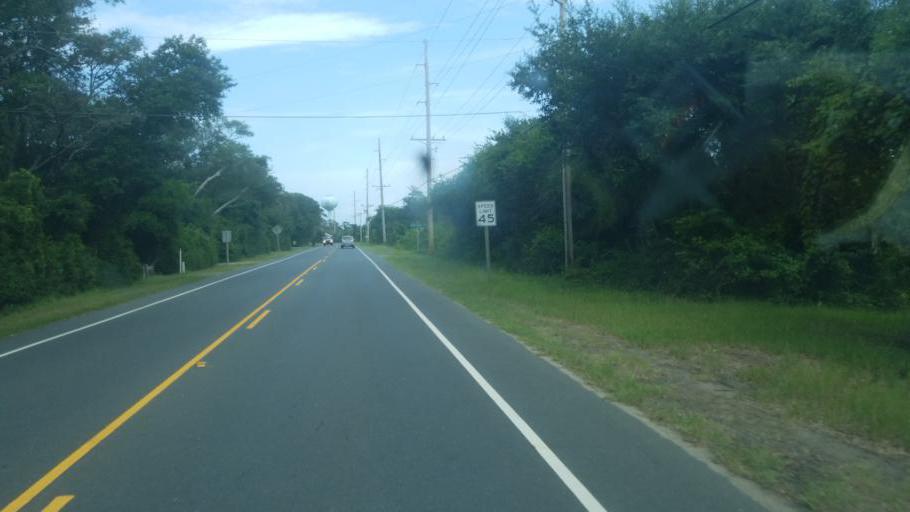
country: US
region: North Carolina
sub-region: Dare County
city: Buxton
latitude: 35.2611
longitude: -75.5789
